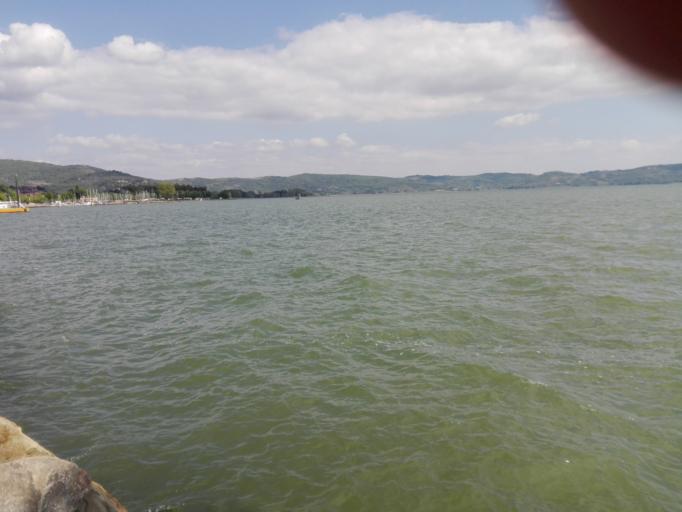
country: IT
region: Umbria
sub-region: Provincia di Perugia
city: Passignano sul Trasimeno
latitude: 43.1834
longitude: 12.1386
